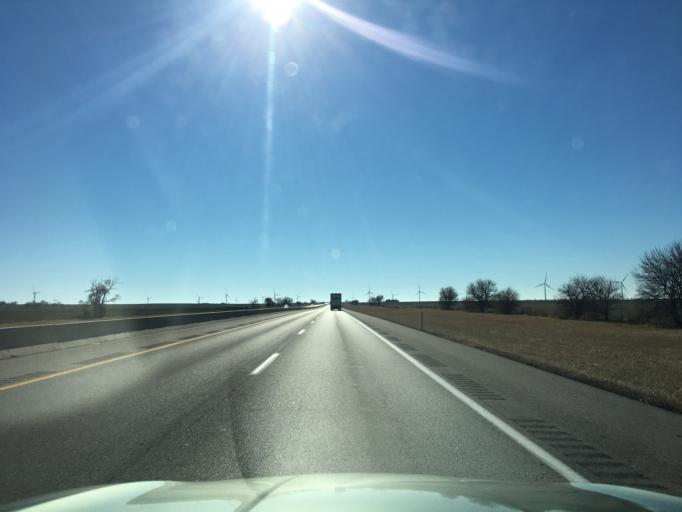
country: US
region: Kansas
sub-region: Sumner County
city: Wellington
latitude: 37.1783
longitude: -97.3396
